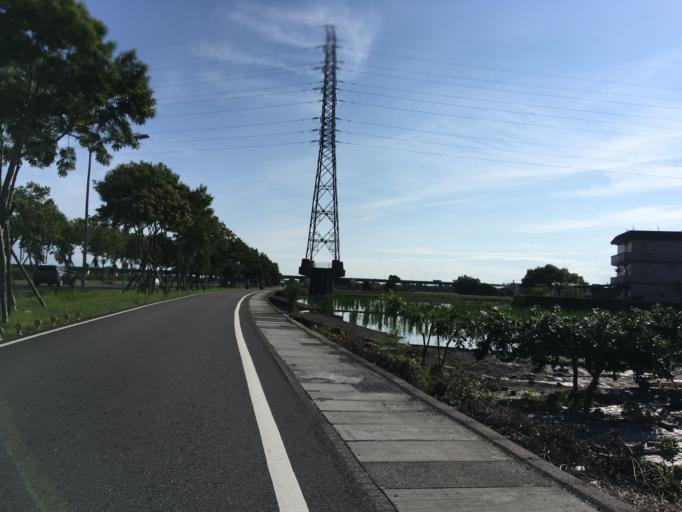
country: TW
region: Taiwan
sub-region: Yilan
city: Yilan
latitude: 24.6789
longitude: 121.7871
